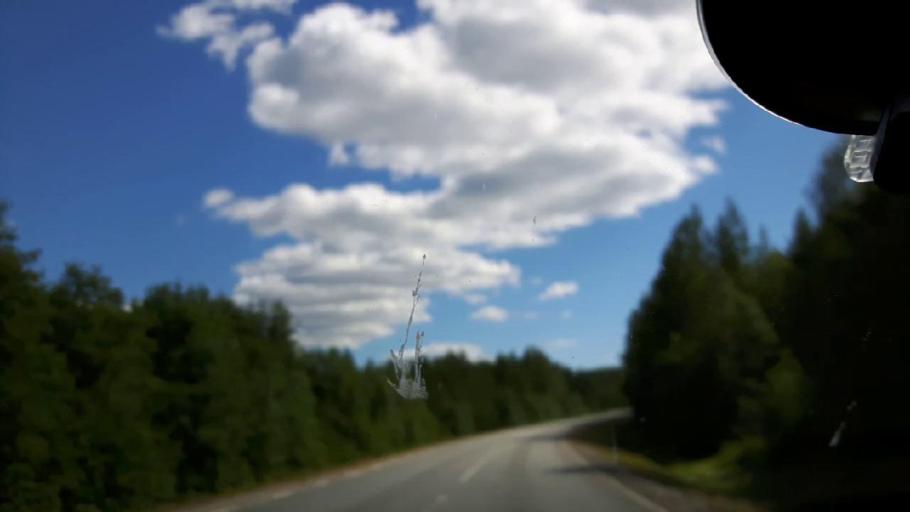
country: SE
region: Vaesternorrland
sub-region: Ange Kommun
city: Fransta
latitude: 62.8196
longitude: 16.2005
